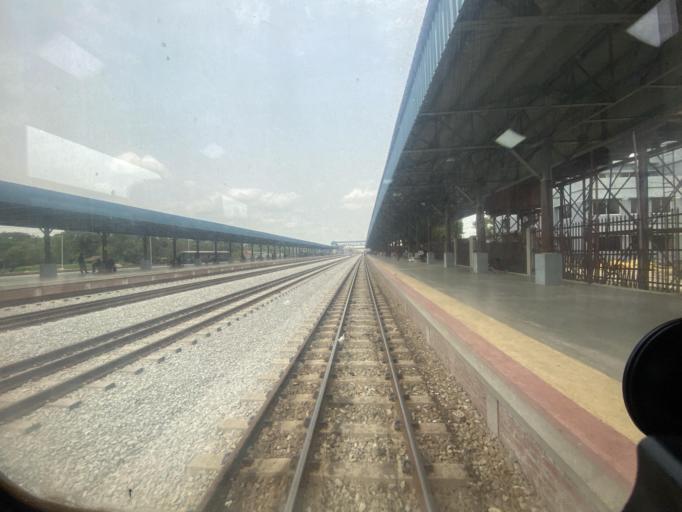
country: BD
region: Chittagong
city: Comilla
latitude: 23.4625
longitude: 91.1669
